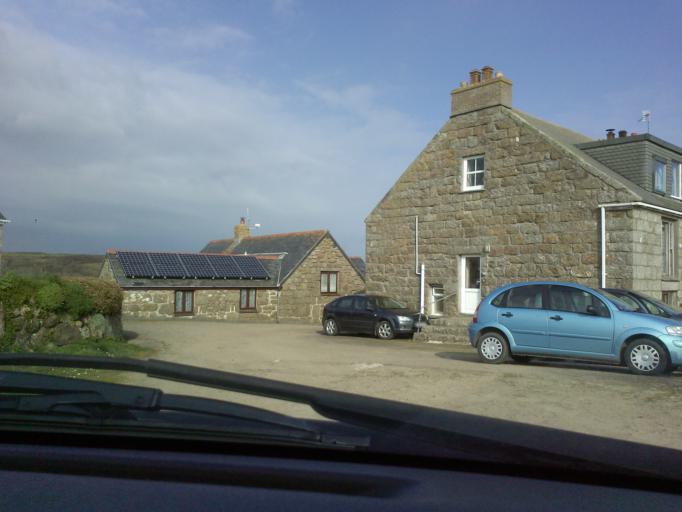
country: GB
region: England
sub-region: Cornwall
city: St. Buryan
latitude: 50.0441
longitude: -5.6569
